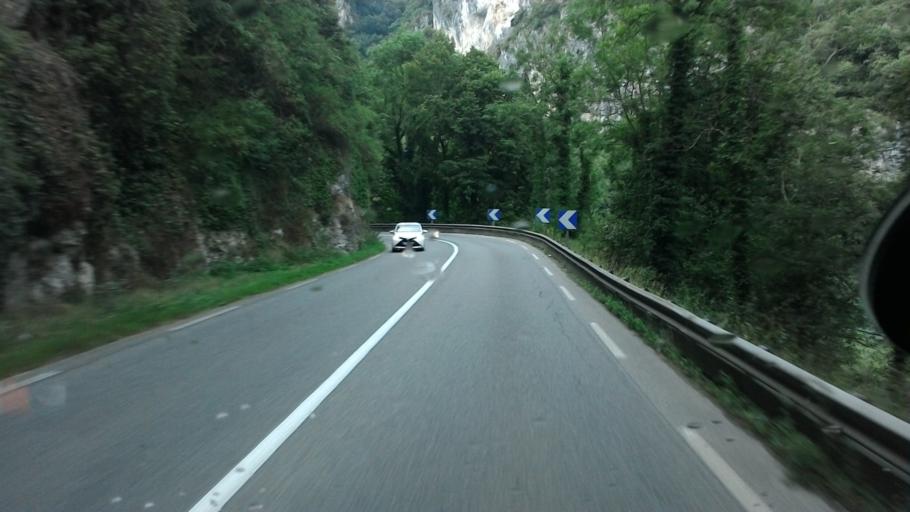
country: FR
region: Rhone-Alpes
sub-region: Departement de la Savoie
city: Yenne
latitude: 45.7091
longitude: 5.7318
